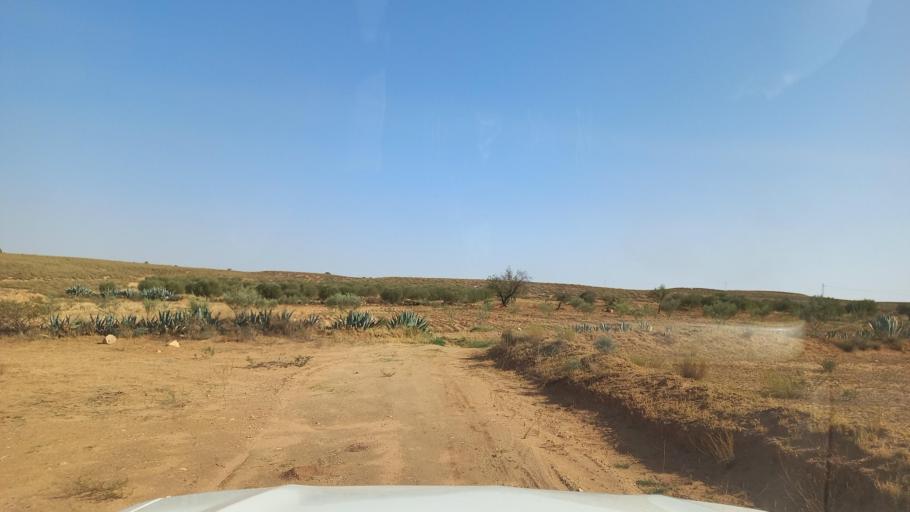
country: TN
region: Al Qasrayn
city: Kasserine
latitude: 35.2034
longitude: 8.9733
